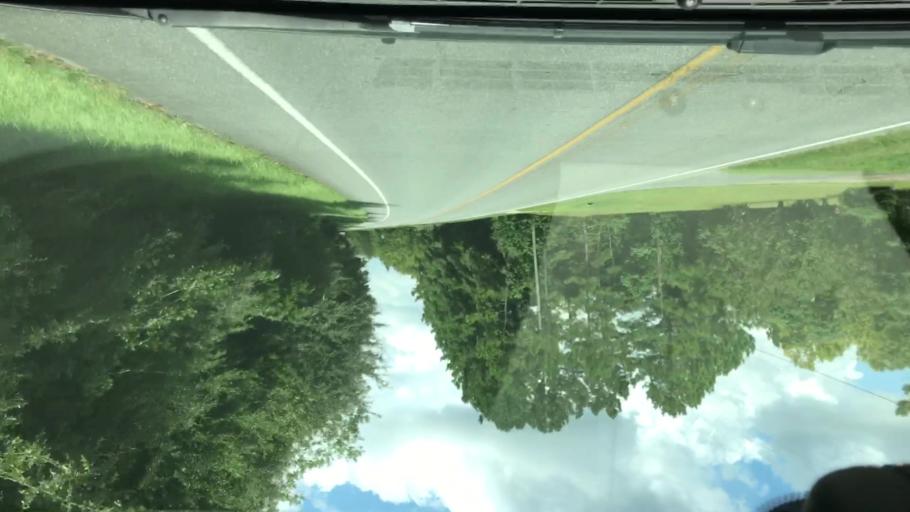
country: US
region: Florida
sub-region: Jackson County
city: Malone
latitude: 30.8831
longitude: -85.1592
